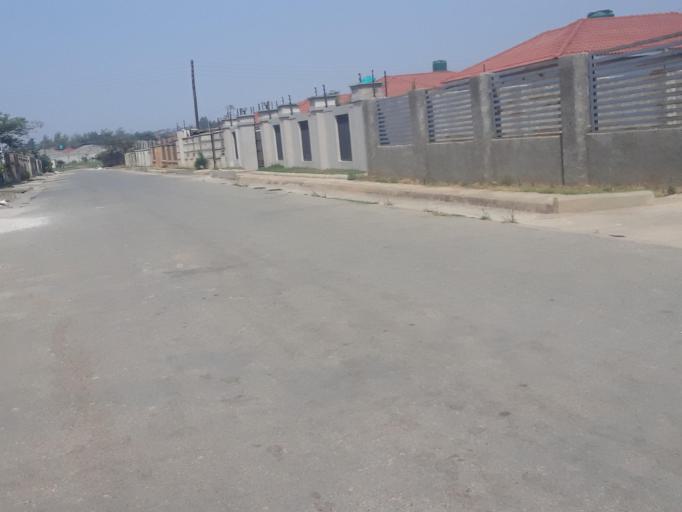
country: ZM
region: Lusaka
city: Lusaka
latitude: -15.3650
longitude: 28.2883
